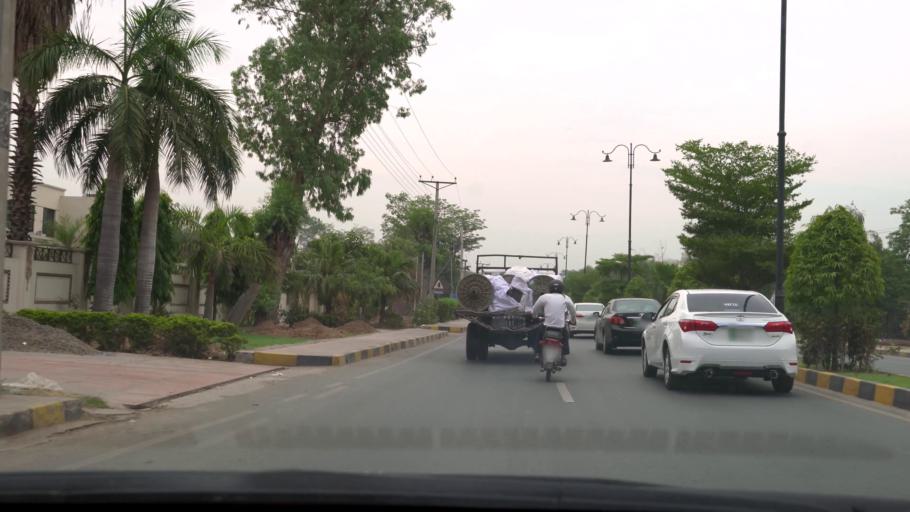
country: PK
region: Punjab
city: Faisalabad
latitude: 31.4289
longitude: 73.0853
